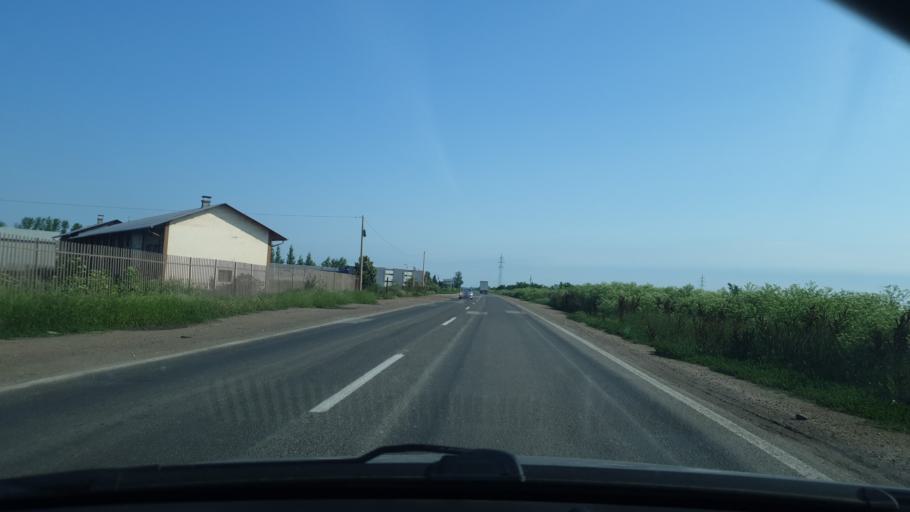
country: RS
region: Central Serbia
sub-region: Podunavski Okrug
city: Smederevo
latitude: 44.6558
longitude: 20.9686
